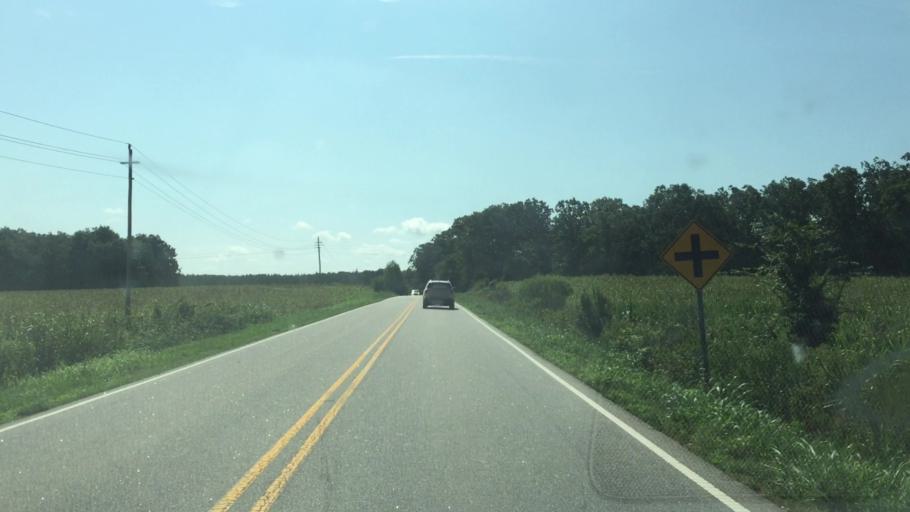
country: US
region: North Carolina
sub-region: Anson County
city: Burnsville
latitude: 35.0997
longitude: -80.3120
